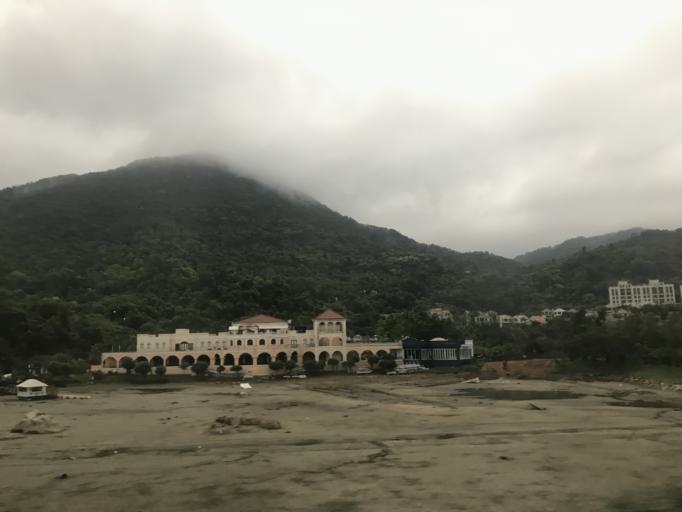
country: HK
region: Tai Po
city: Tai Po
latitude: 22.4377
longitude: 114.1893
